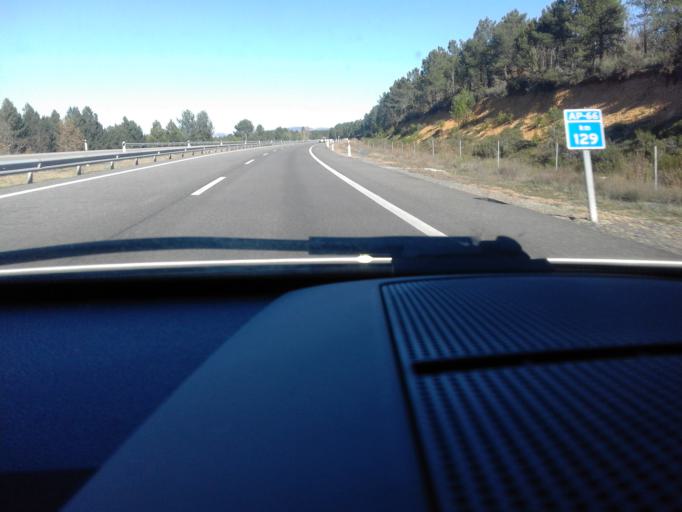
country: ES
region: Castille and Leon
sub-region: Provincia de Leon
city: Cimanes del Tejar
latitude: 42.6615
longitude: -5.7511
